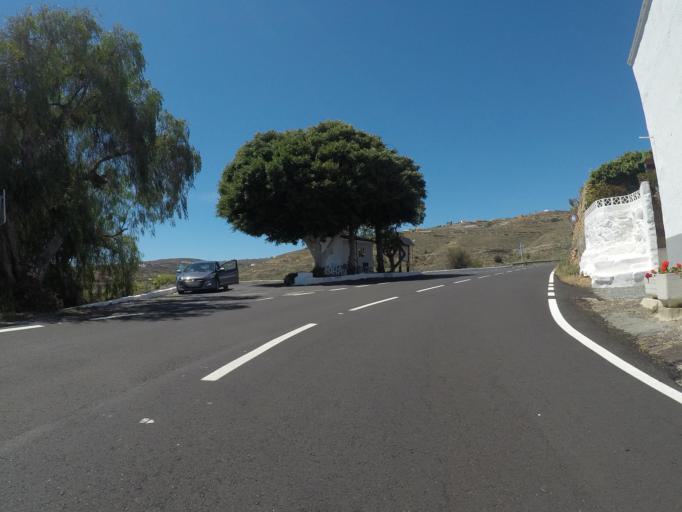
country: ES
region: Canary Islands
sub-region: Provincia de Santa Cruz de Tenerife
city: Lomo de Arico
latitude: 28.1790
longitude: -16.4825
